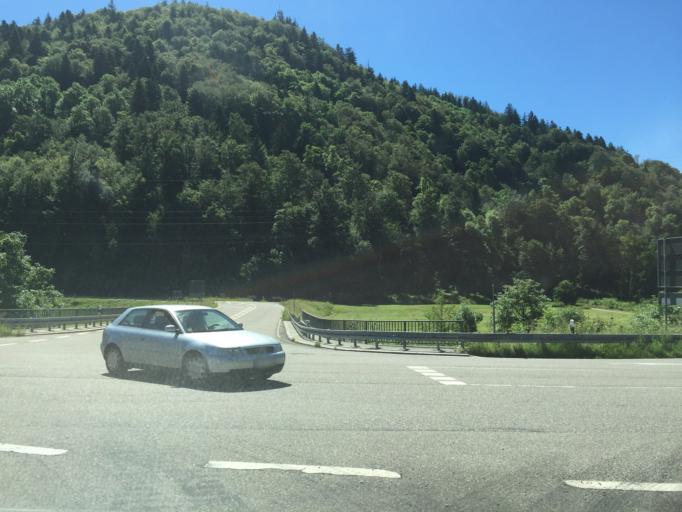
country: DE
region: Baden-Wuerttemberg
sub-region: Freiburg Region
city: Aitern
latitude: 47.7985
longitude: 7.9052
